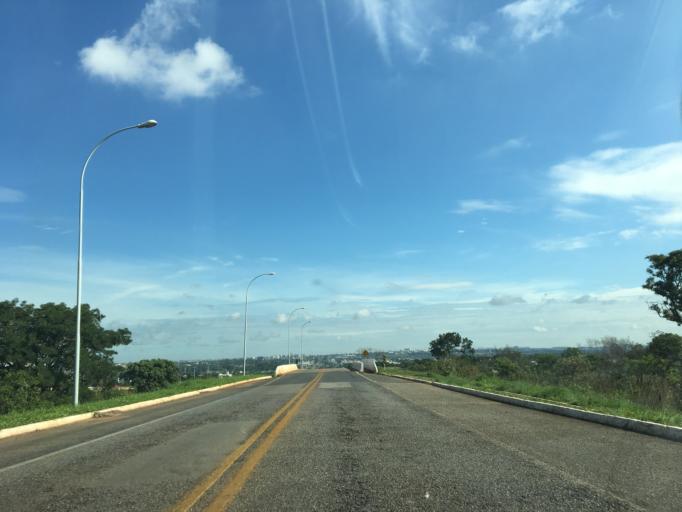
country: BR
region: Federal District
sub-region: Brasilia
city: Brasilia
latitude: -15.8849
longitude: -47.9596
